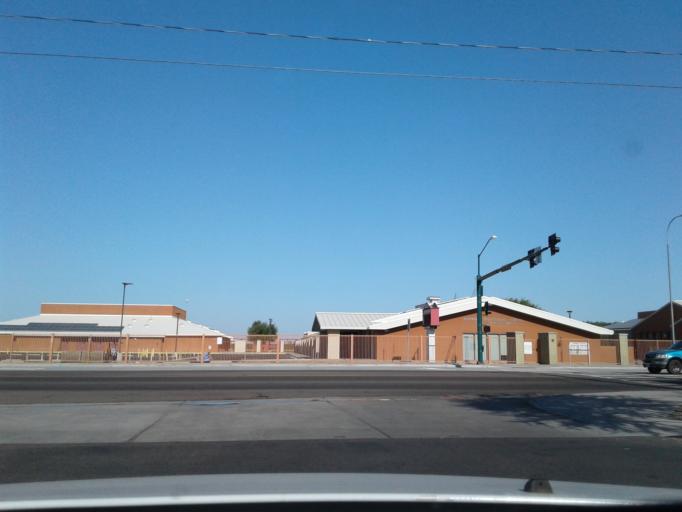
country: US
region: Arizona
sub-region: Maricopa County
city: Laveen
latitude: 33.4335
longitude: -112.1690
